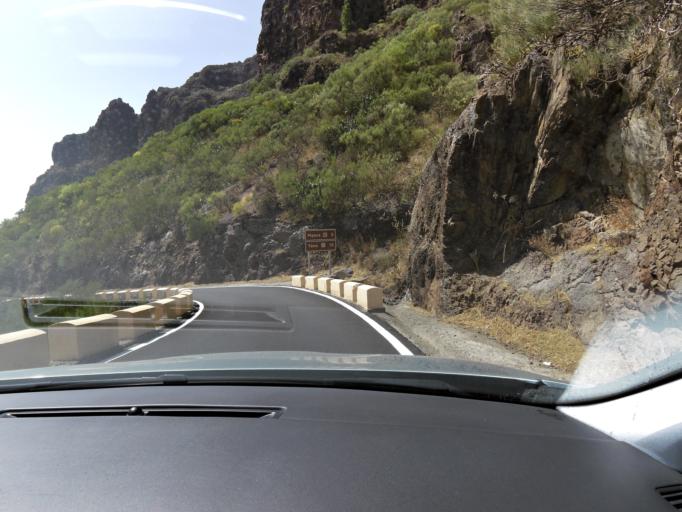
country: ES
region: Canary Islands
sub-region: Provincia de Santa Cruz de Tenerife
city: Santiago del Teide
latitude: 28.3035
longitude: -16.8287
